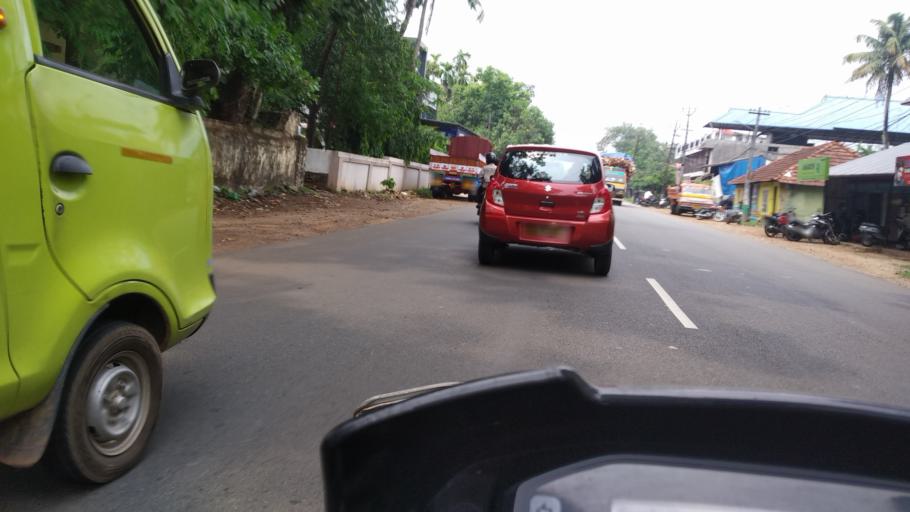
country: IN
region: Kerala
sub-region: Ernakulam
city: Perumpavur
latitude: 10.1163
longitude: 76.4951
